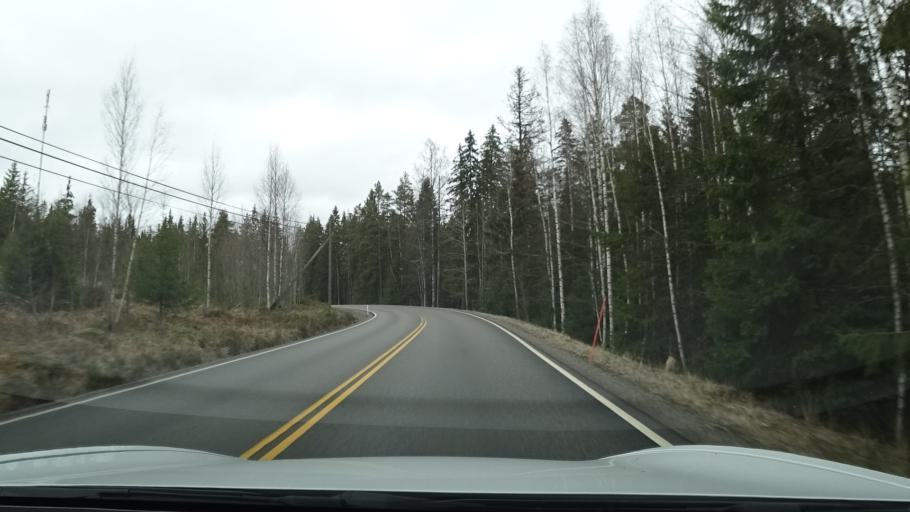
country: FI
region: Uusimaa
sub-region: Porvoo
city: Askola
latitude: 60.5808
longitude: 25.5893
